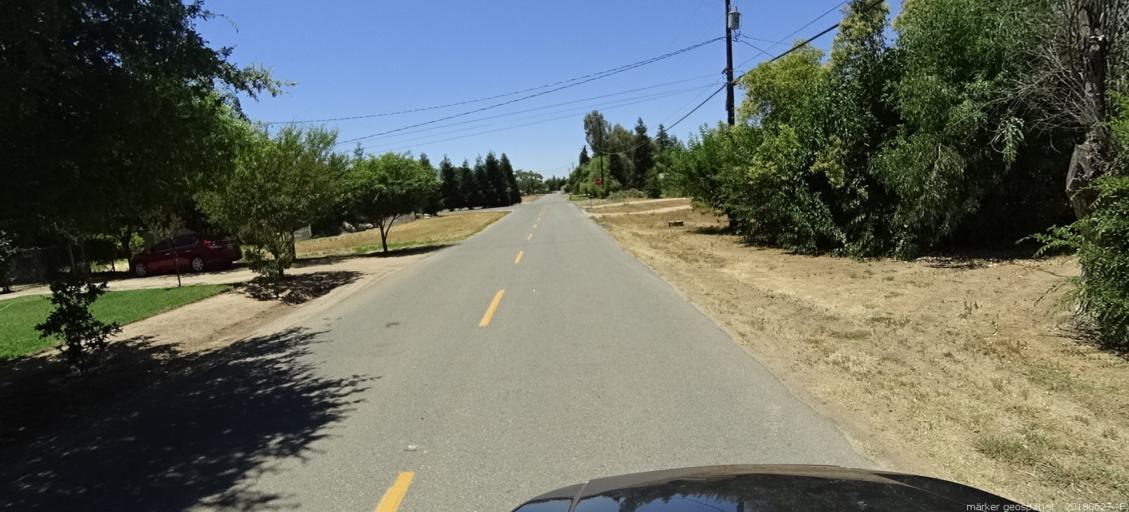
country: US
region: California
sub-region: Madera County
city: Bonadelle Ranchos-Madera Ranchos
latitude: 36.9267
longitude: -119.8725
